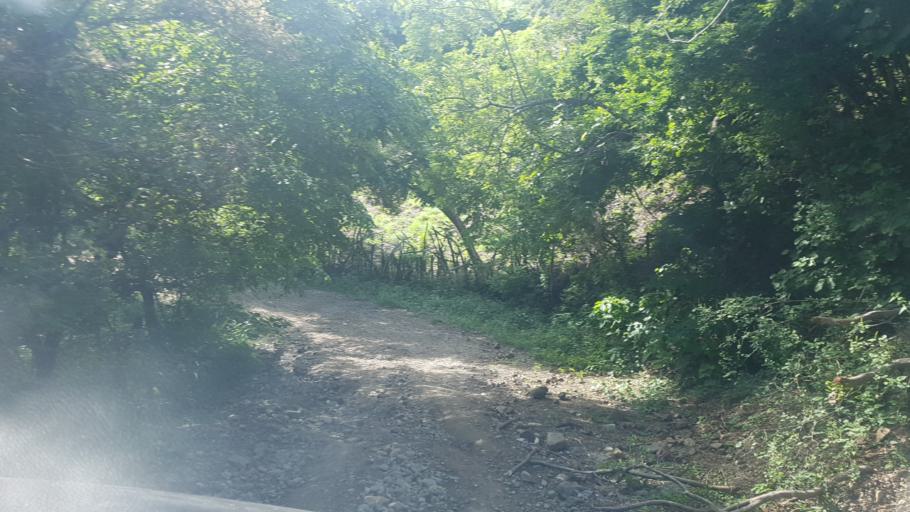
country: NI
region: Nueva Segovia
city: Ocotal
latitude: 13.6074
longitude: -86.4615
